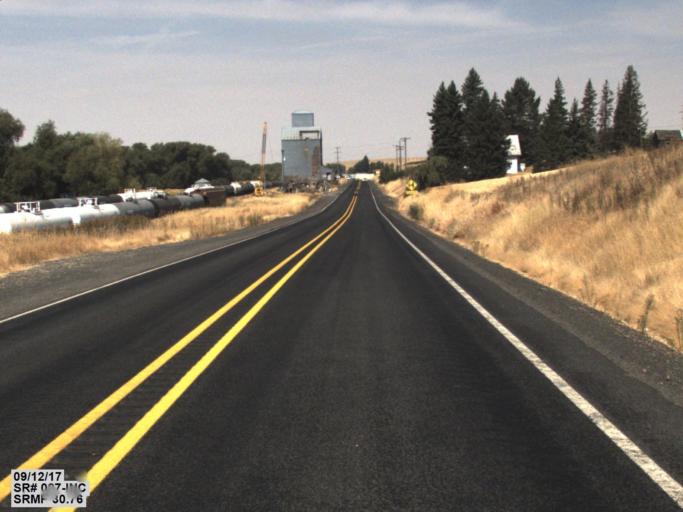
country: US
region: Washington
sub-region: Whitman County
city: Colfax
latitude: 47.0872
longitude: -117.1608
